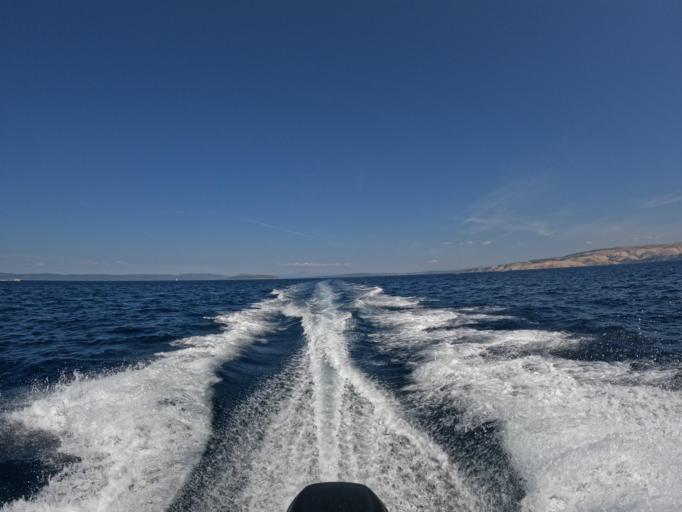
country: HR
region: Primorsko-Goranska
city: Lopar
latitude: 44.8983
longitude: 14.6379
